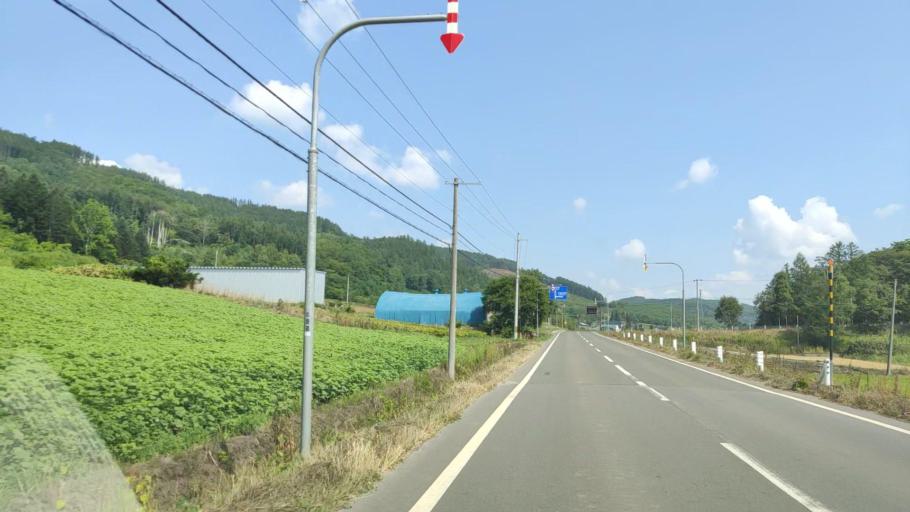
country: JP
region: Hokkaido
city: Shimo-furano
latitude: 43.4334
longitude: 142.4096
